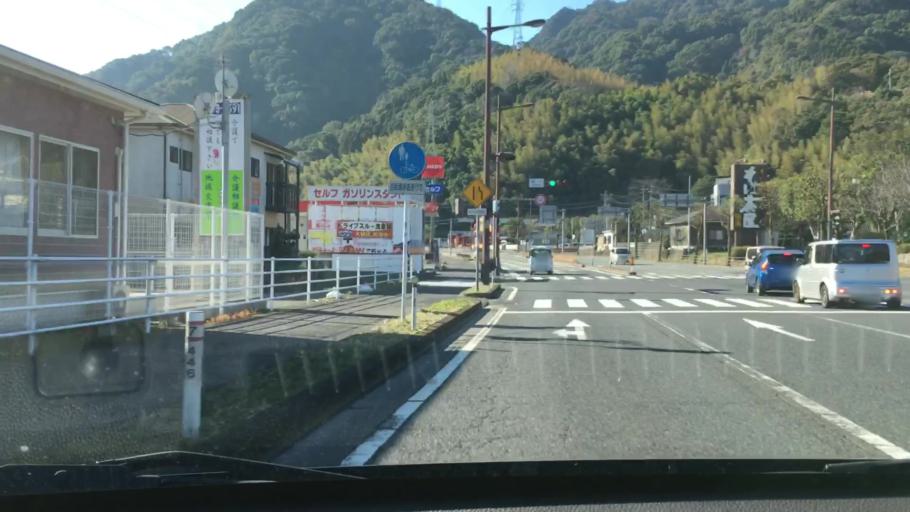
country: JP
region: Kagoshima
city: Kajiki
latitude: 31.7046
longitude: 130.6124
